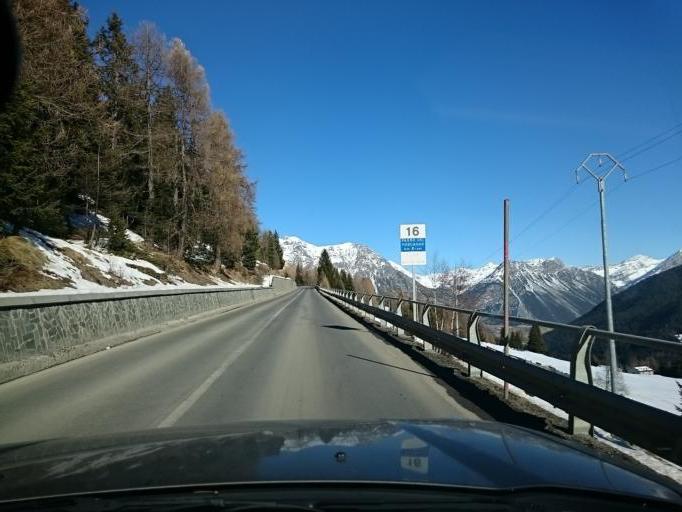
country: IT
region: Lombardy
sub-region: Provincia di Sondrio
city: Isolaccia
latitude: 46.4608
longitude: 10.2434
